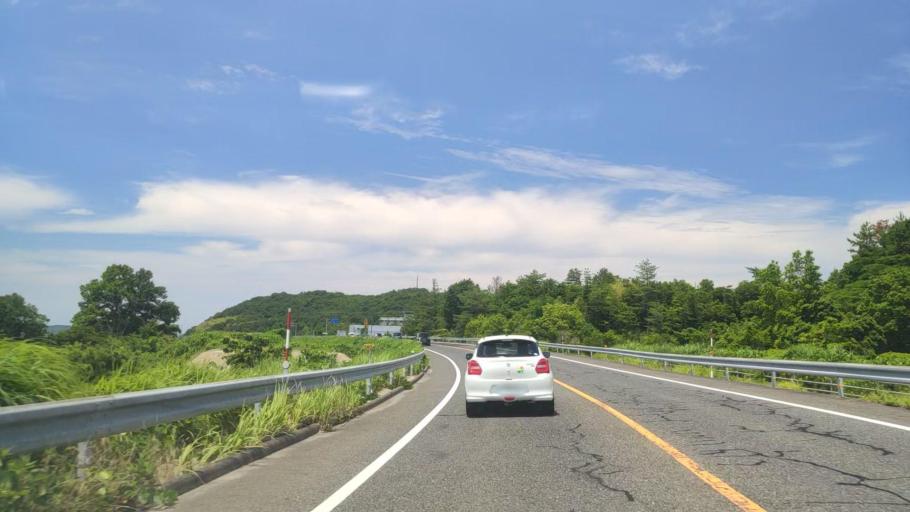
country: JP
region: Tottori
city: Tottori
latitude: 35.4459
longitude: 134.2560
